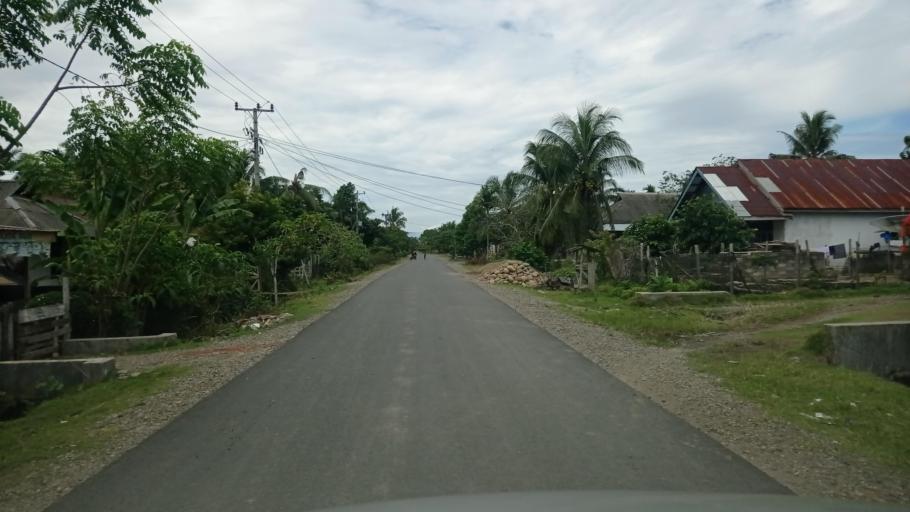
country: ID
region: Jambi
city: Sungai Penuh
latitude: -2.5269
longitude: 101.0805
